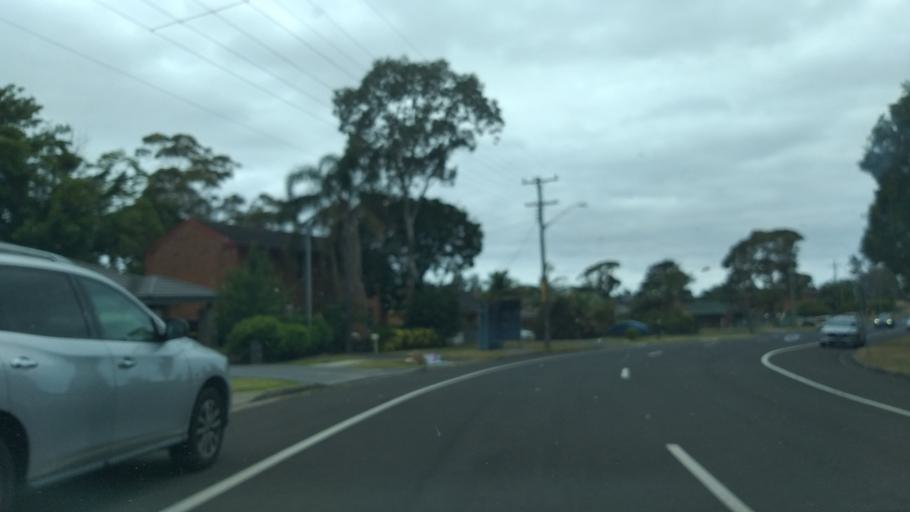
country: AU
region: New South Wales
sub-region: Wollongong
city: Berkeley
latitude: -34.4787
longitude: 150.8476
